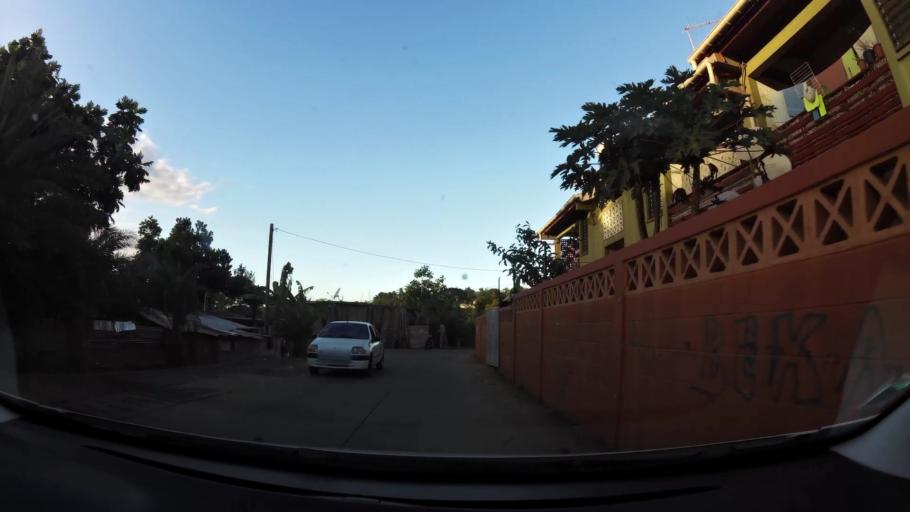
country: YT
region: Koungou
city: Koungou
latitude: -12.7352
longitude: 45.1986
